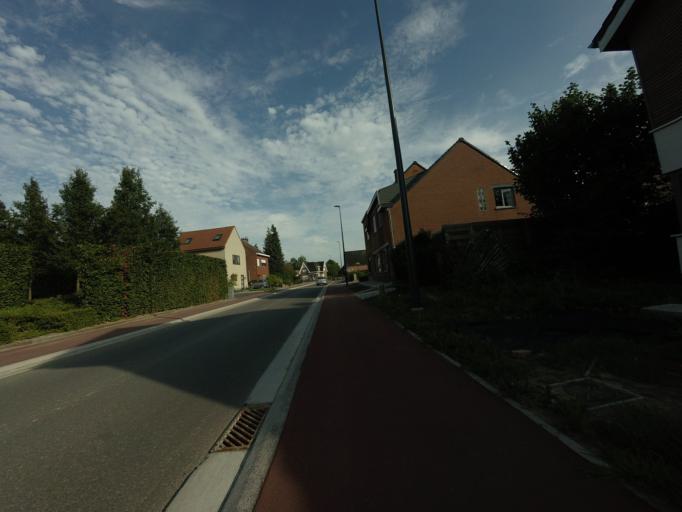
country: BE
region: Flanders
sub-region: Provincie Vlaams-Brabant
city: Boortmeerbeek
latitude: 50.9739
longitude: 4.5763
